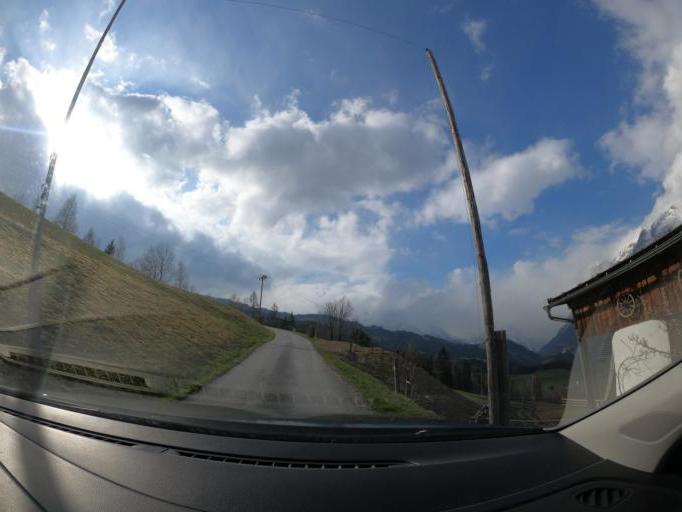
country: AT
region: Salzburg
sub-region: Politischer Bezirk Sankt Johann im Pongau
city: Pfarrwerfen
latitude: 47.4581
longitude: 13.1938
